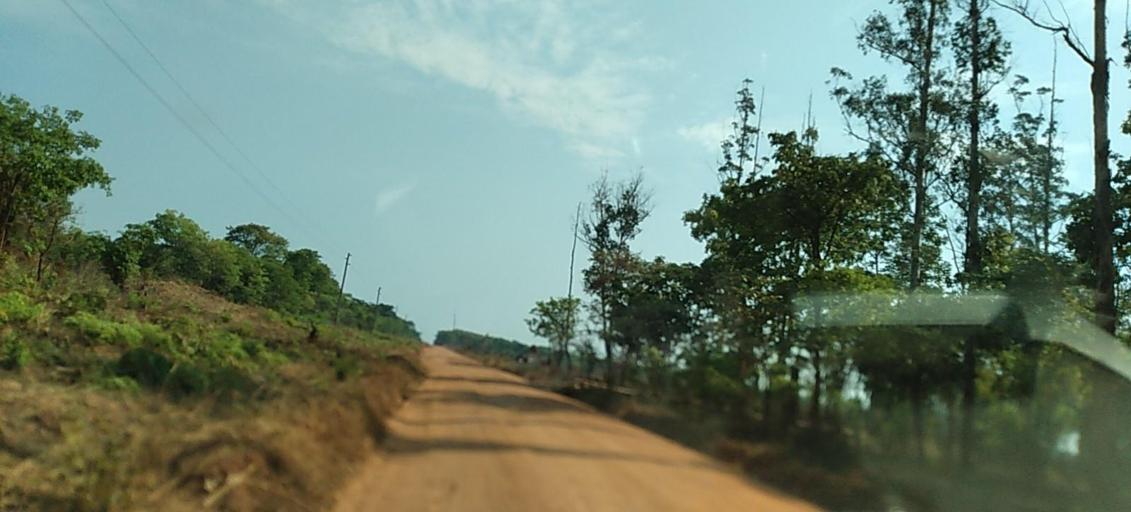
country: ZM
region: Copperbelt
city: Kalulushi
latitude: -12.9964
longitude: 27.8142
